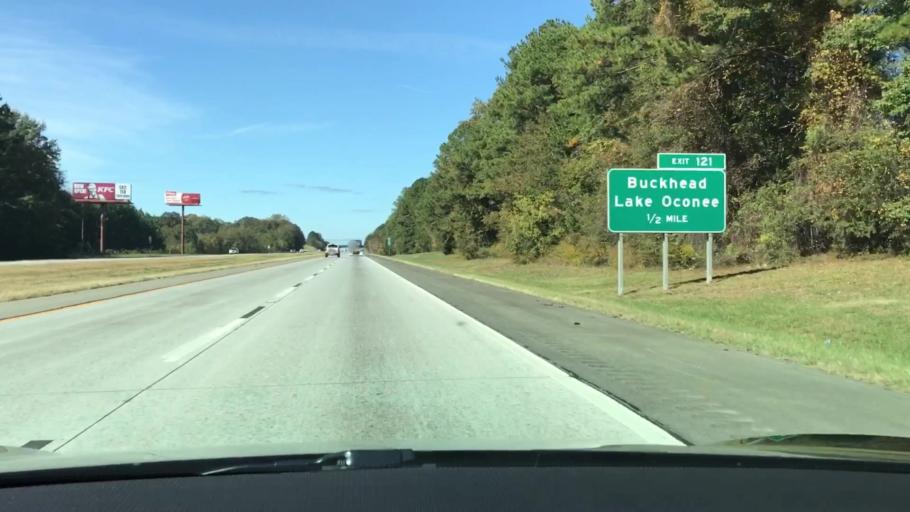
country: US
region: Georgia
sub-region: Putnam County
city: Jefferson
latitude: 33.5477
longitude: -83.3428
